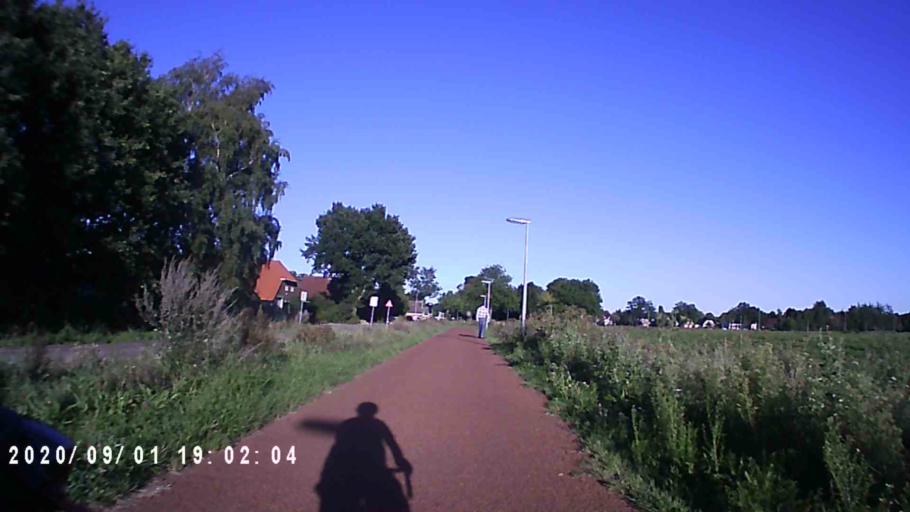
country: NL
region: Groningen
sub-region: Gemeente Veendam
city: Veendam
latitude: 53.1179
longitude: 6.8678
